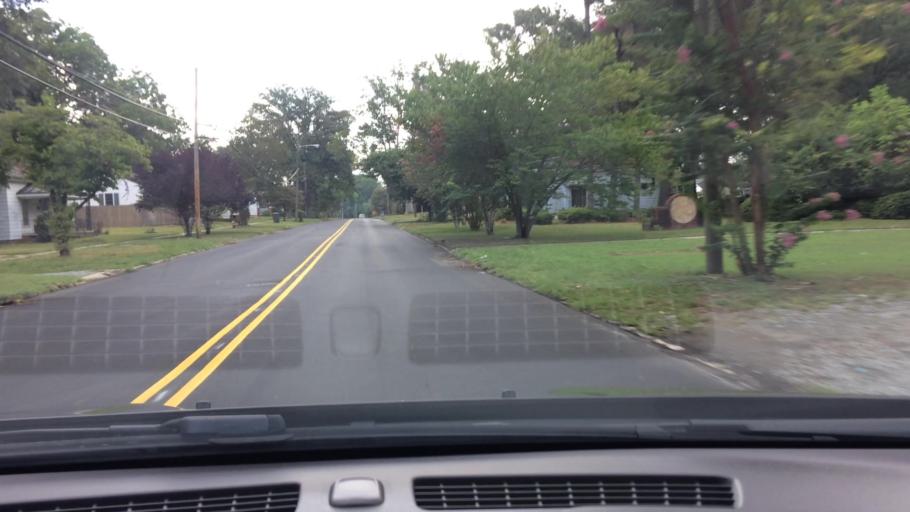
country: US
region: North Carolina
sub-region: Pitt County
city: Ayden
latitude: 35.4708
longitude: -77.4114
